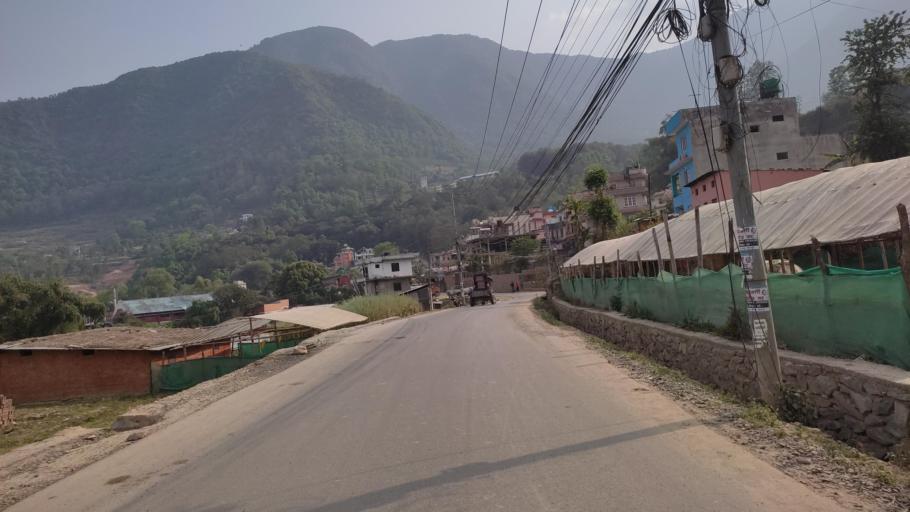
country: NP
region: Central Region
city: Kirtipur
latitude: 27.6657
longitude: 85.2587
